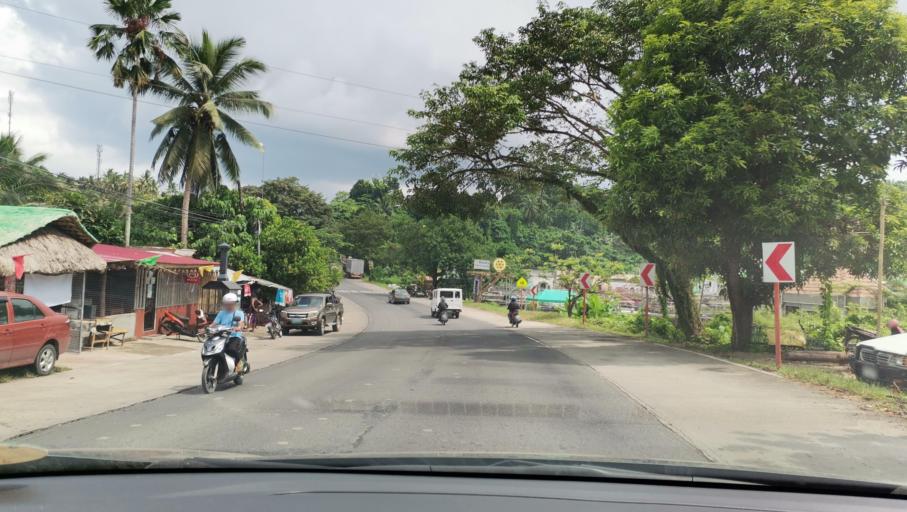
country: PH
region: Calabarzon
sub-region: Province of Quezon
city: Rizal
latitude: 13.9503
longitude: 122.2885
